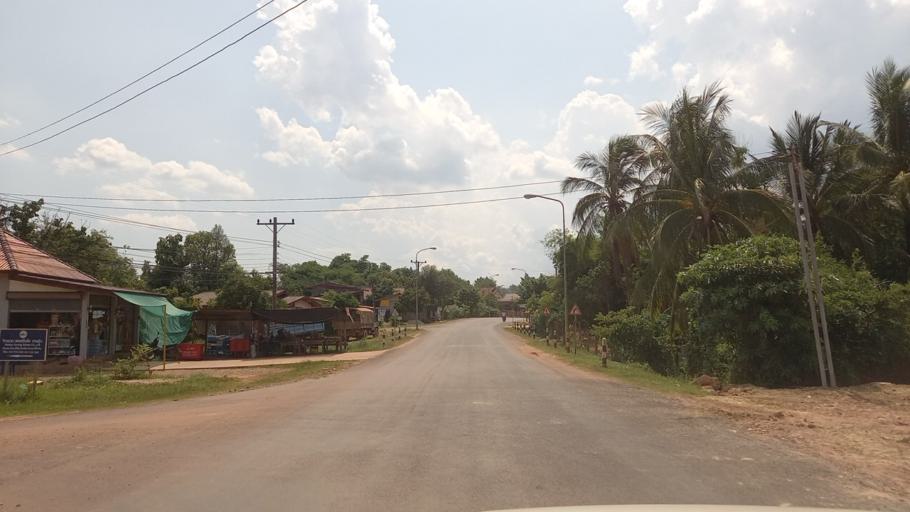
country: LA
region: Bolikhamxai
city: Muang Pakxan
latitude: 18.4173
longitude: 103.6389
